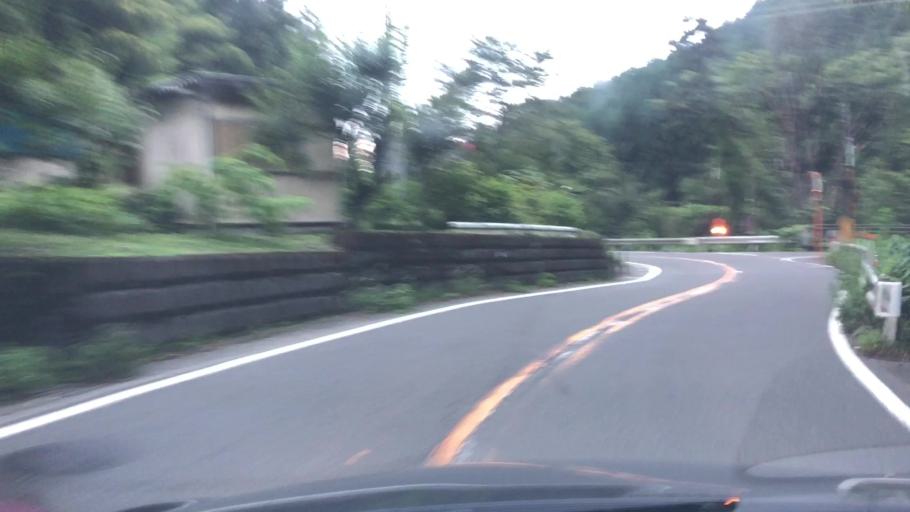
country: JP
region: Tokyo
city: Ome
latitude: 35.7634
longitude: 139.2284
